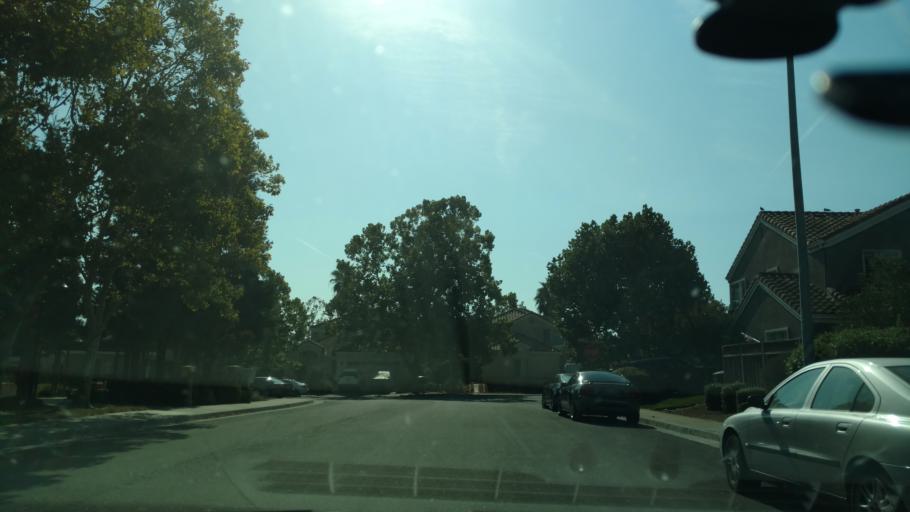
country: US
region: California
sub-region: Santa Clara County
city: San Martin
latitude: 37.0942
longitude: -121.6430
